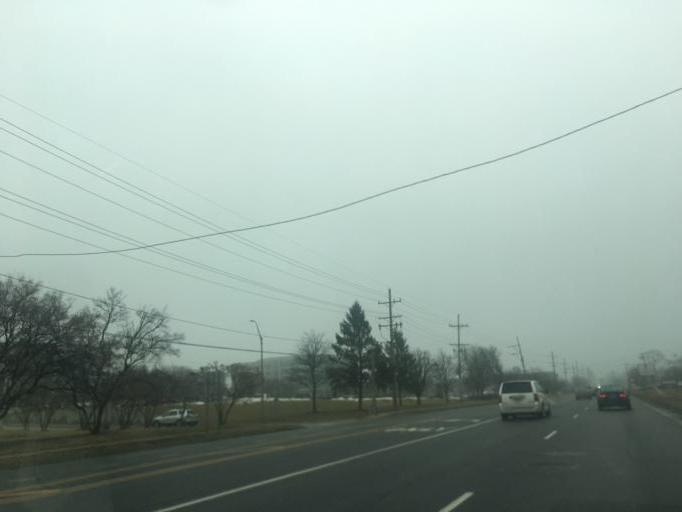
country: US
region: Illinois
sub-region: DuPage County
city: Lisle
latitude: 41.8040
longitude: -88.0522
